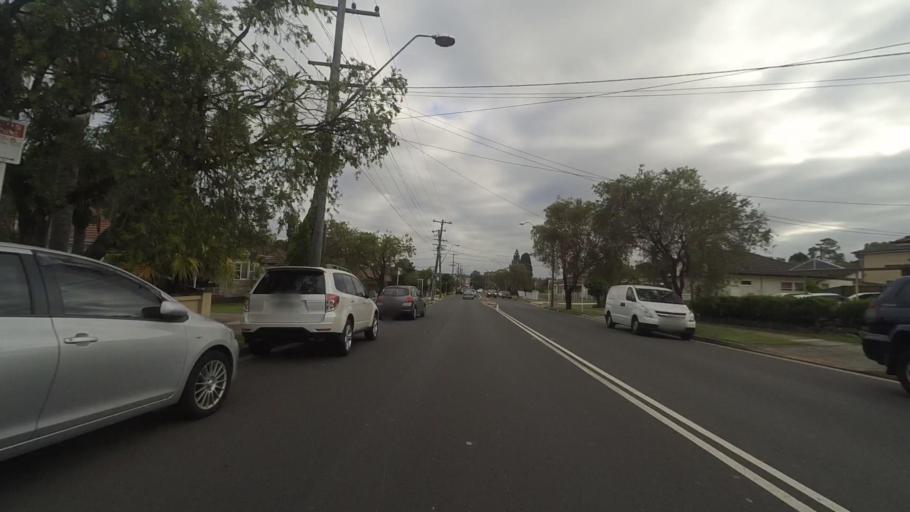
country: AU
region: New South Wales
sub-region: Bankstown
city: Revesby
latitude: -33.9283
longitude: 151.0120
